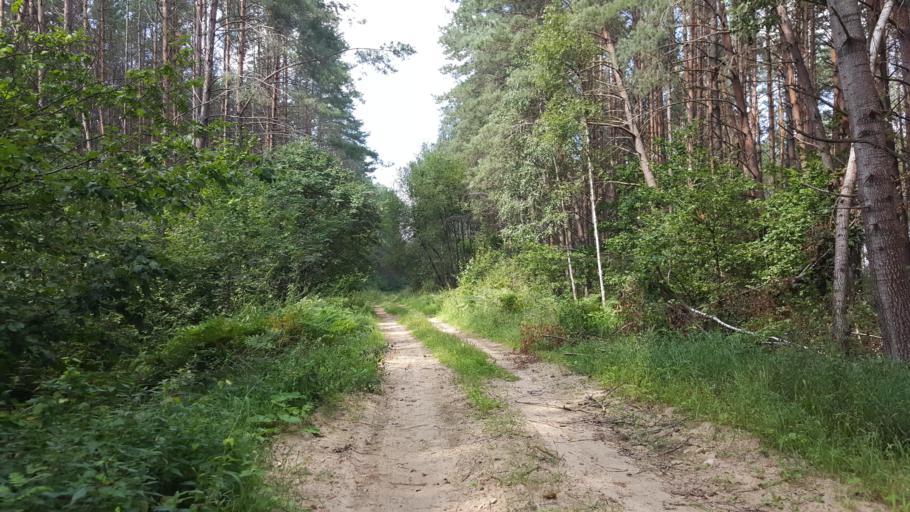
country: PL
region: Podlasie
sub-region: Powiat hajnowski
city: Hajnowka
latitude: 52.5719
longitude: 23.5918
